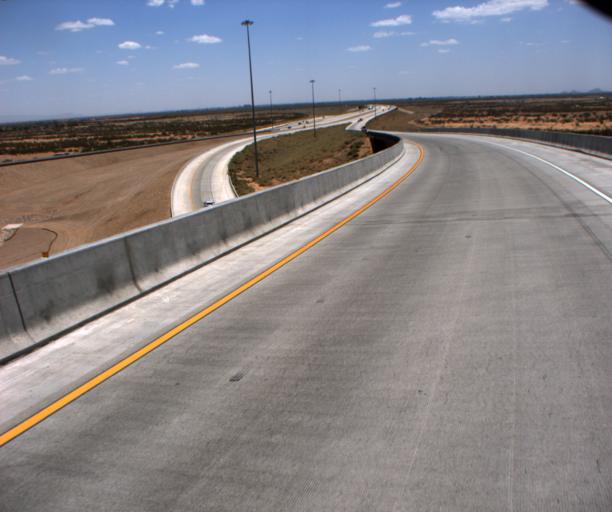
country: US
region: Arizona
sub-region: Maricopa County
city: Queen Creek
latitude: 33.3298
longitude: -111.6506
